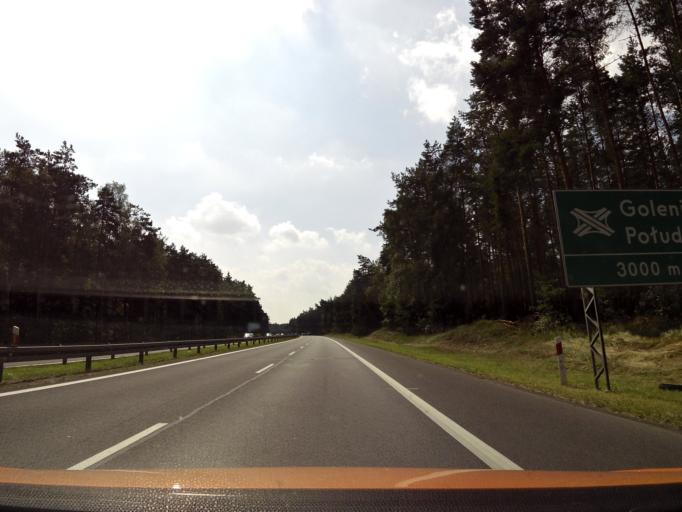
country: PL
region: West Pomeranian Voivodeship
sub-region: Powiat goleniowski
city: Goleniow
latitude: 53.5617
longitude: 14.7956
